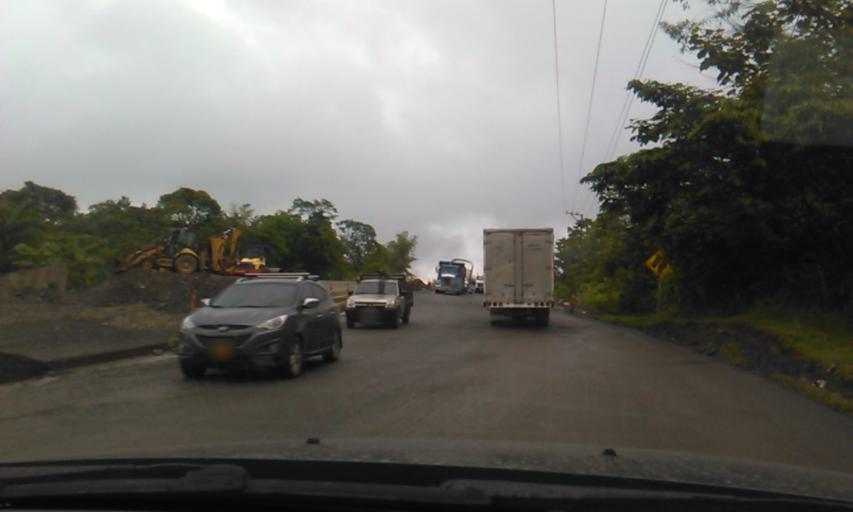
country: CO
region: Valle del Cauca
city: Buenaventura
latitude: 3.8751
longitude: -76.8887
